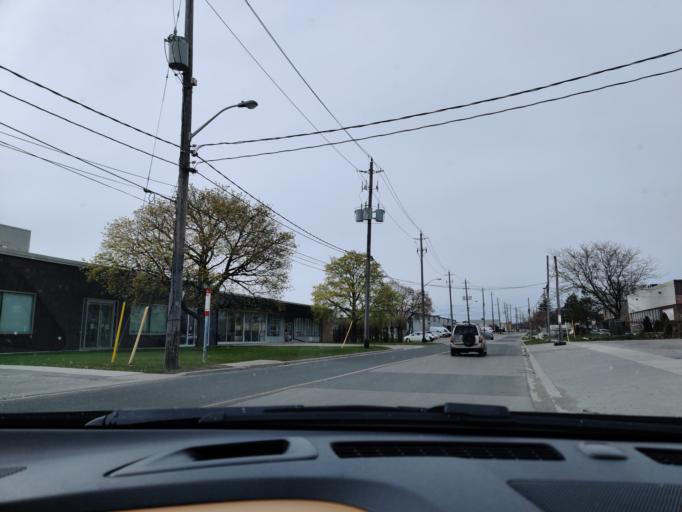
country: CA
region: Ontario
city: Toronto
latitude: 43.7032
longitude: -79.4699
